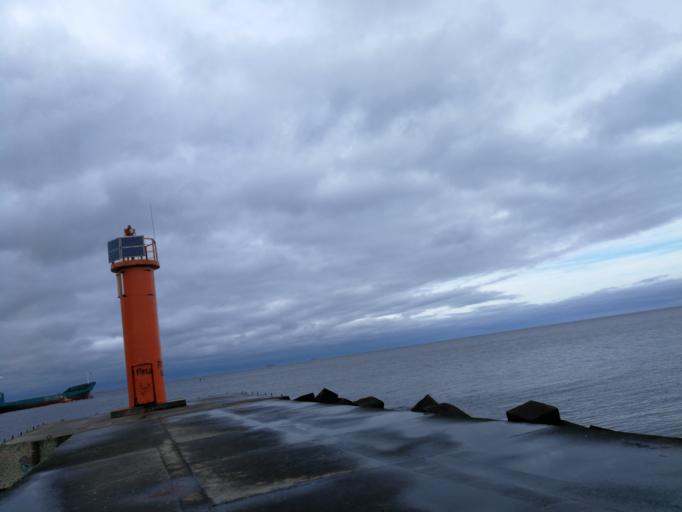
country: LV
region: Riga
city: Daugavgriva
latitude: 57.0682
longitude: 24.0153
